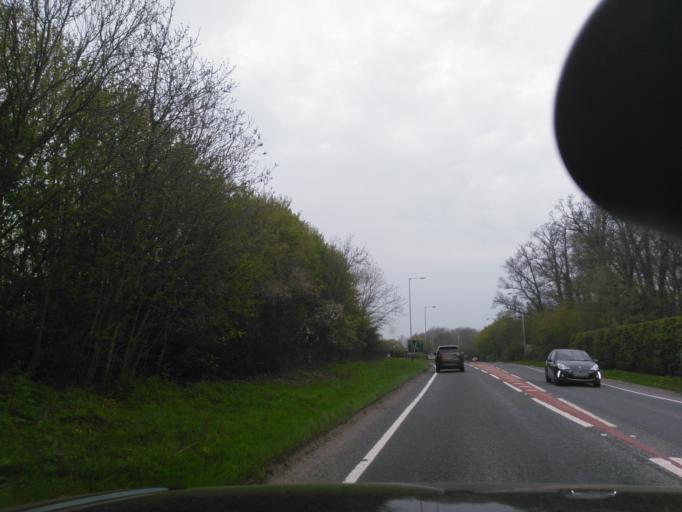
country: GB
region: England
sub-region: Somerset
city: Frome
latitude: 51.2099
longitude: -2.3144
